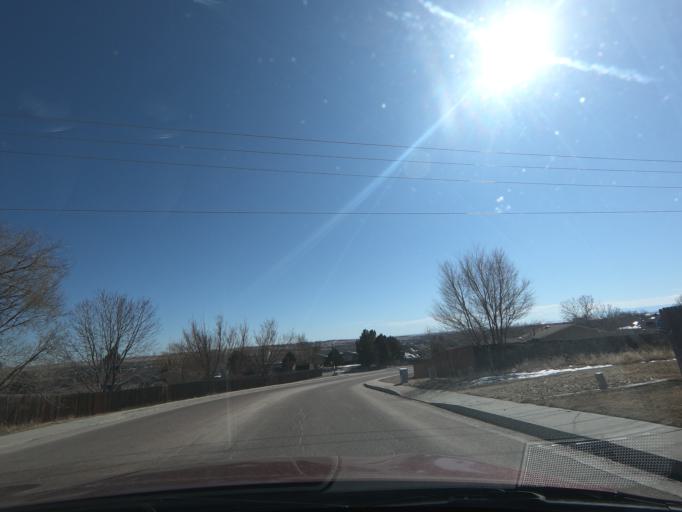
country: US
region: Colorado
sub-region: El Paso County
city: Security-Widefield
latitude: 38.7228
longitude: -104.6898
